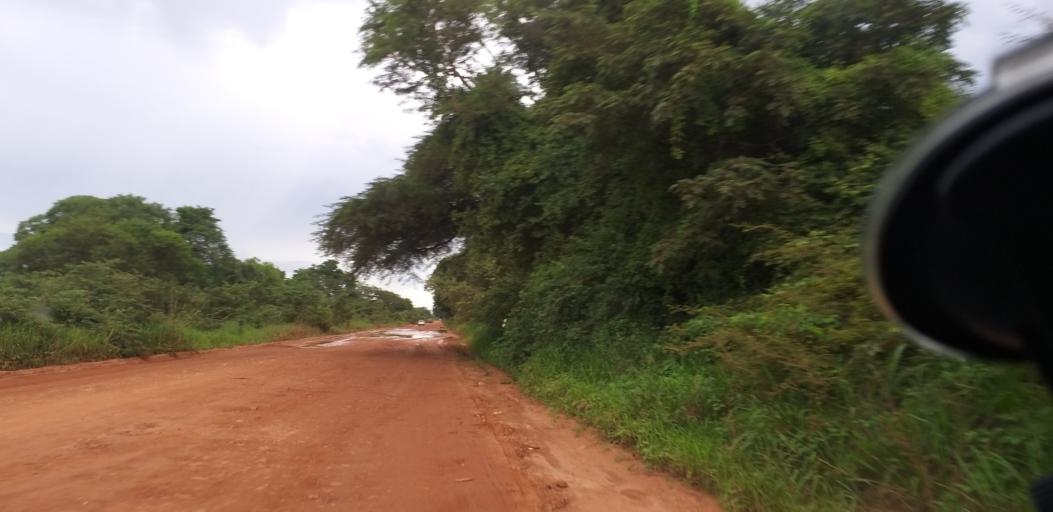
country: ZM
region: Lusaka
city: Lusaka
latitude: -15.2129
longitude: 28.4337
